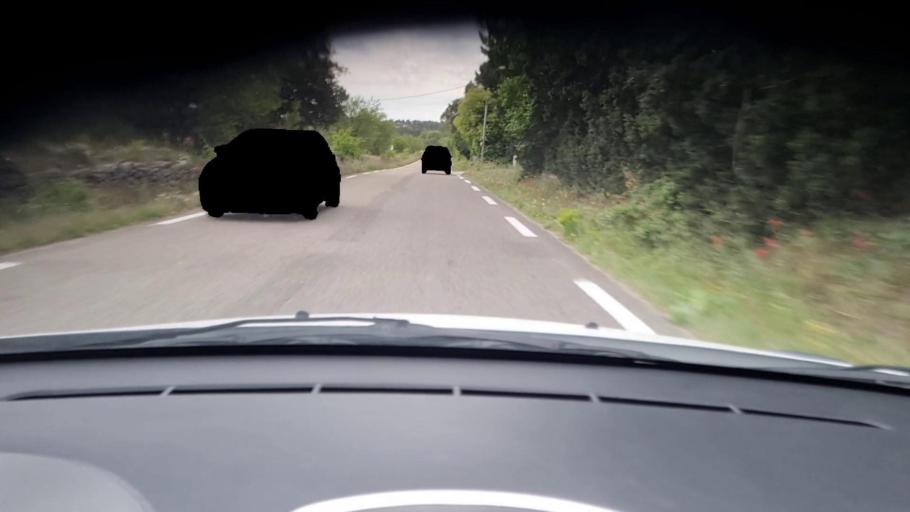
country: FR
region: Languedoc-Roussillon
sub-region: Departement du Gard
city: Uzes
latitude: 43.9891
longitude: 4.4122
